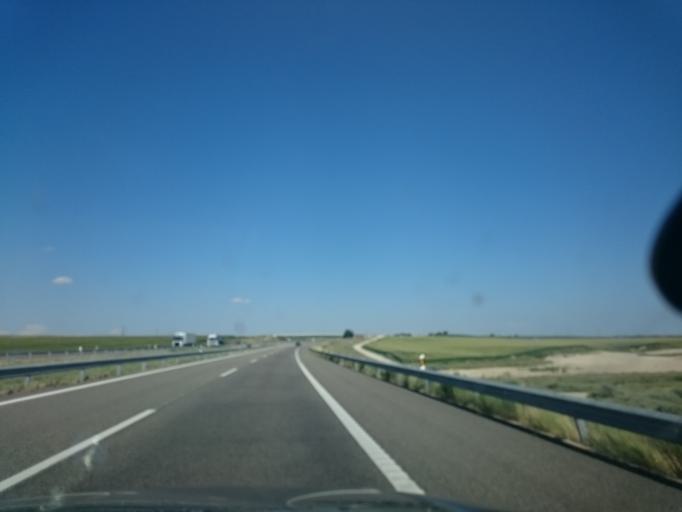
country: ES
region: Aragon
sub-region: Provincia de Huesca
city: Valfarta
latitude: 41.5194
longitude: -0.1165
